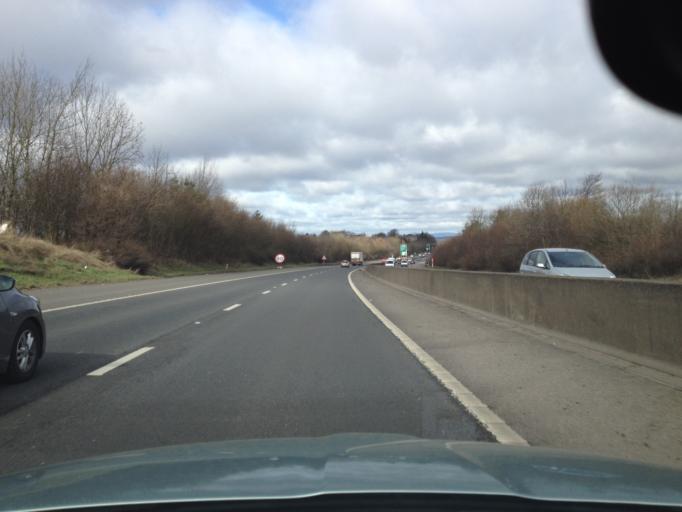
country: GB
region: Scotland
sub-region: Edinburgh
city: Colinton
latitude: 55.9018
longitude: -3.2715
